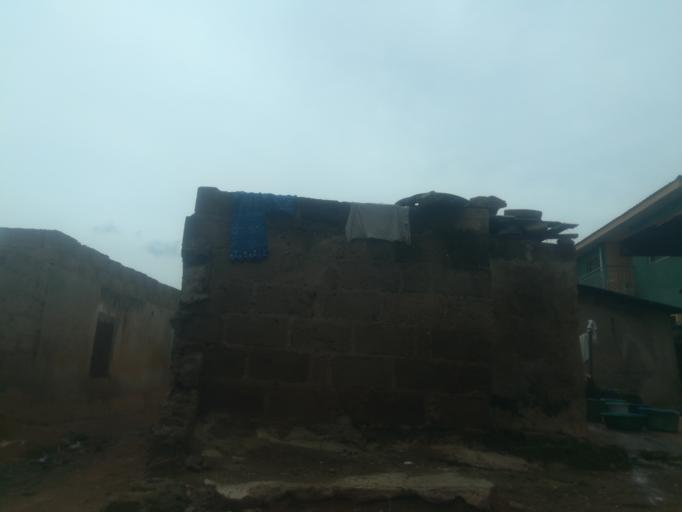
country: NG
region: Oyo
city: Ibadan
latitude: 7.3796
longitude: 3.9320
